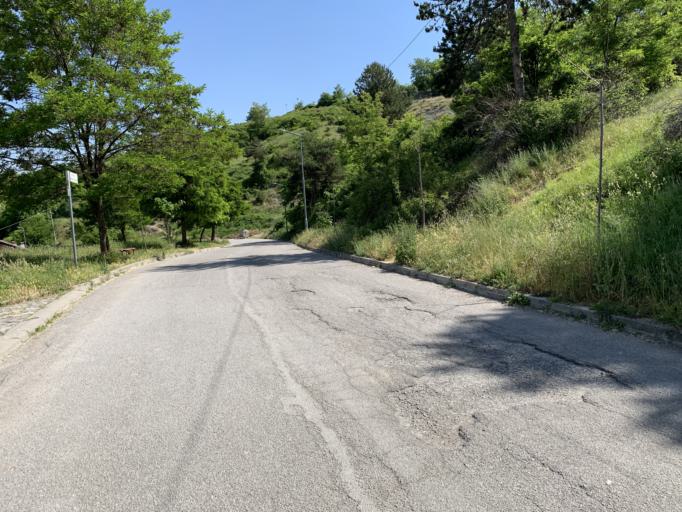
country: AL
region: Korce
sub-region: Rrethi i Korces
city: Korce
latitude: 40.6168
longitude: 20.7877
